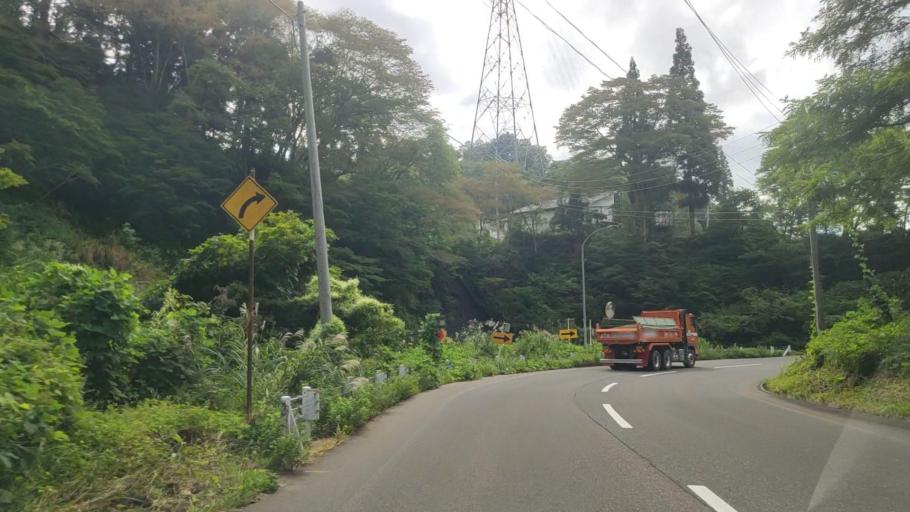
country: JP
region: Nagano
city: Iiyama
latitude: 36.8906
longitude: 138.3238
